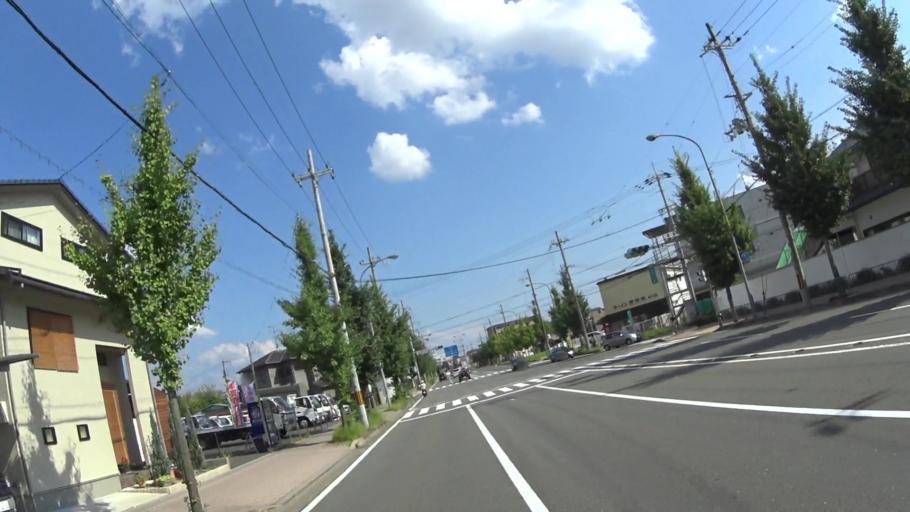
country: JP
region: Kyoto
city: Muko
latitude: 34.9840
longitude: 135.7077
